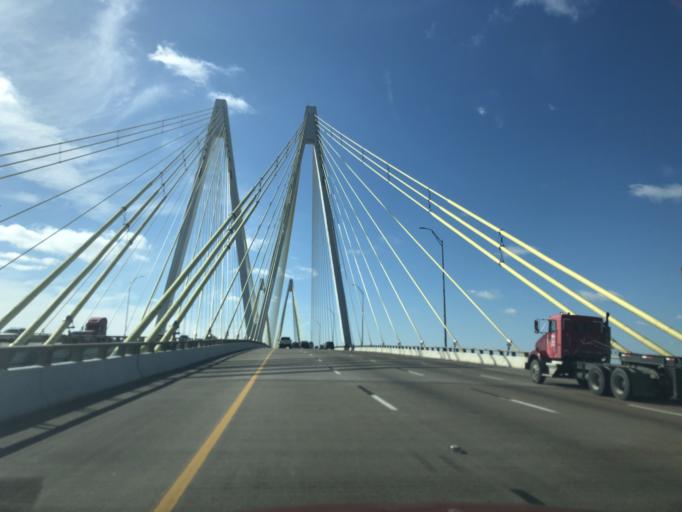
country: US
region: Texas
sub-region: Harris County
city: La Porte
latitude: 29.7062
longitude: -95.0139
